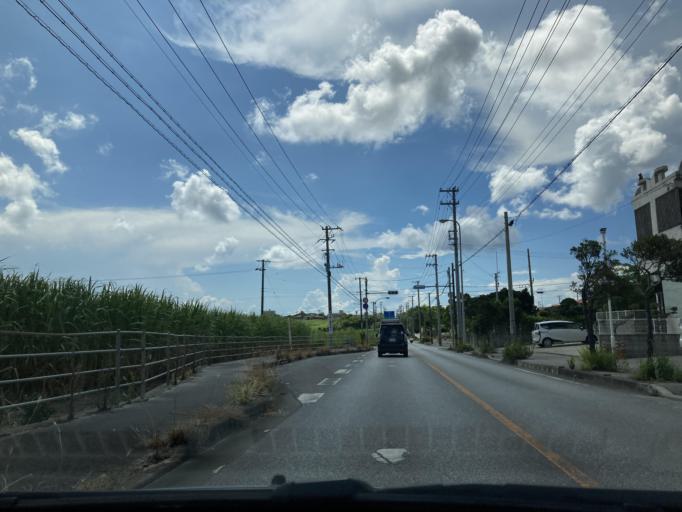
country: JP
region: Okinawa
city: Itoman
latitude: 26.1387
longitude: 127.7292
